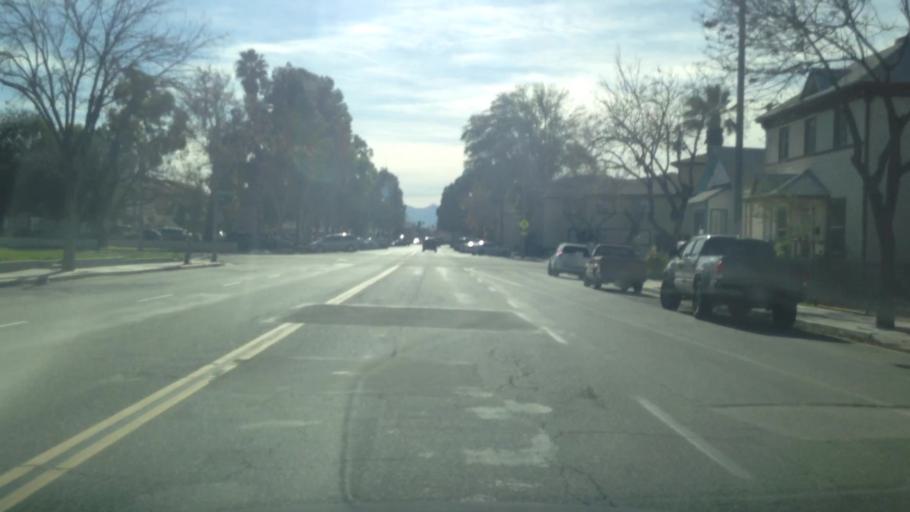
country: US
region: California
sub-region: Riverside County
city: Rubidoux
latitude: 33.9838
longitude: -117.3687
